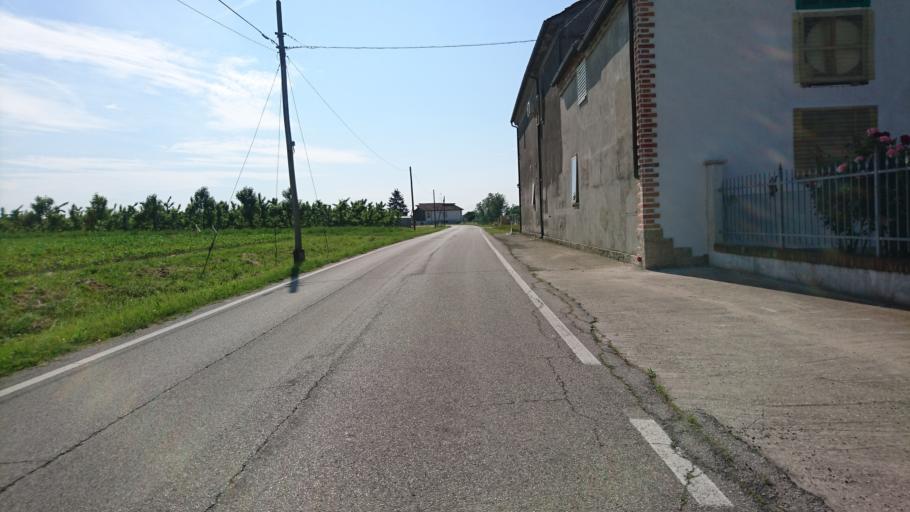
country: IT
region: Veneto
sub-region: Provincia di Padova
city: Merlara
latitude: 45.1704
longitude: 11.4465
